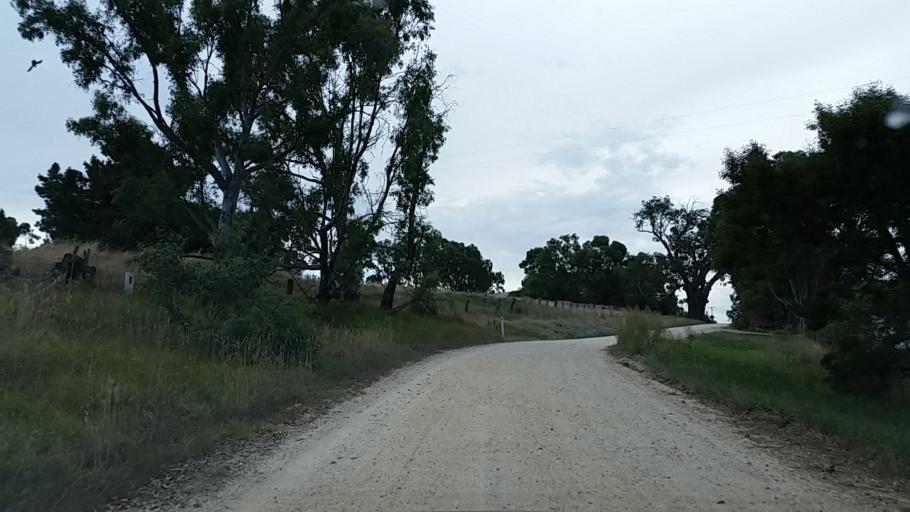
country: AU
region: South Australia
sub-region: Barossa
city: Angaston
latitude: -34.5641
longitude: 139.0792
